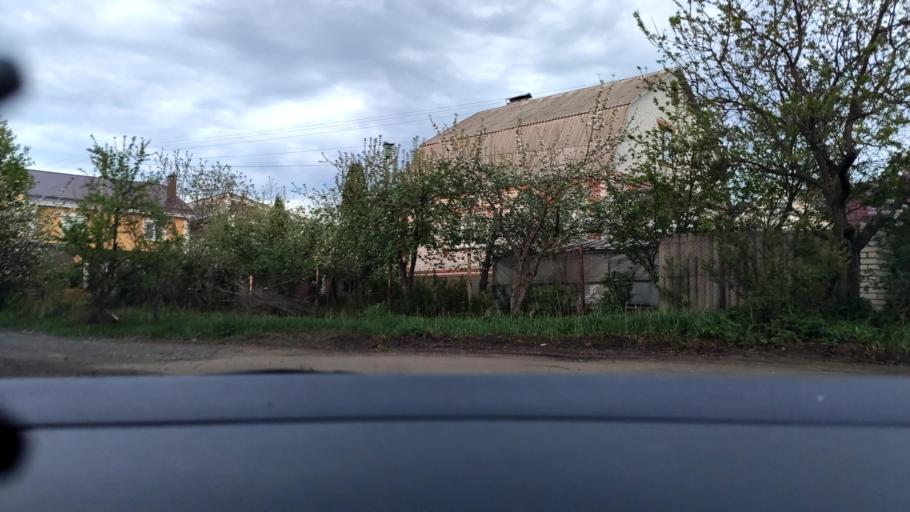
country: RU
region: Voronezj
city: Podgornoye
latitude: 51.7350
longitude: 39.1659
